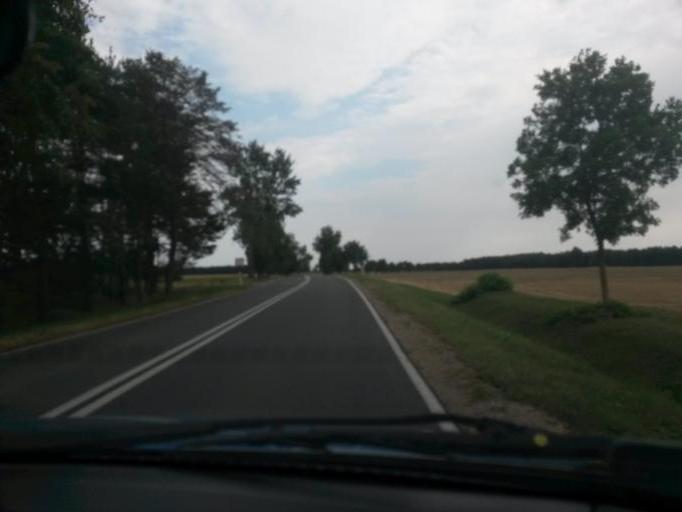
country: PL
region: Masovian Voivodeship
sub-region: Powiat zurominski
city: Lubowidz
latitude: 53.0933
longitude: 19.8625
